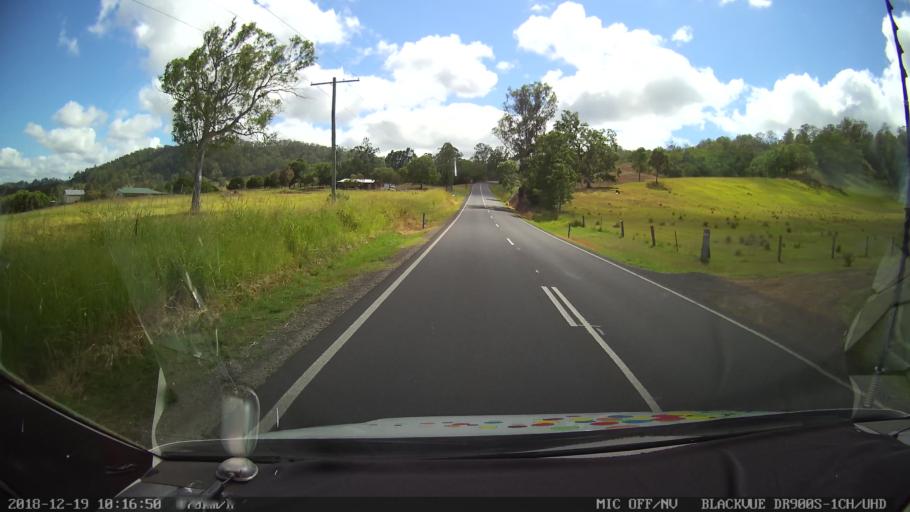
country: AU
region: New South Wales
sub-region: Kyogle
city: Kyogle
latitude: -28.6059
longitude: 153.0254
